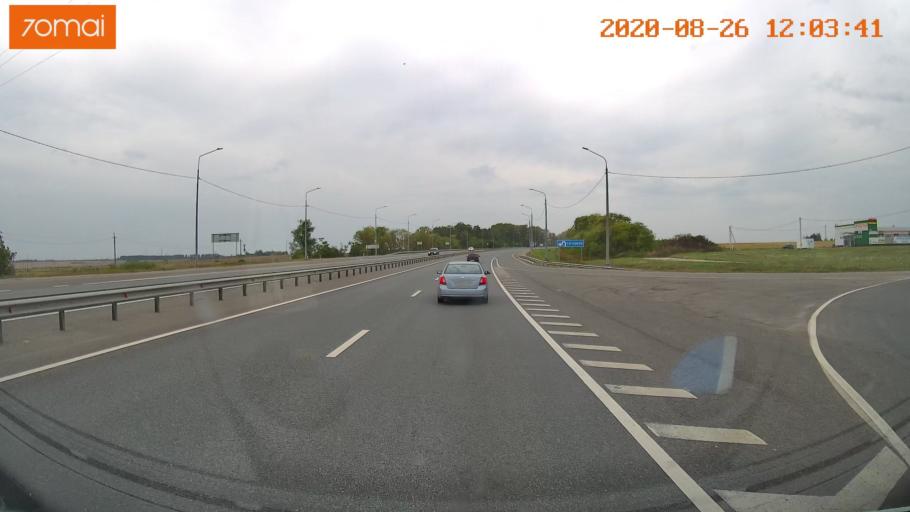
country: RU
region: Rjazan
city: Kiritsy
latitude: 54.3024
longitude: 40.2015
